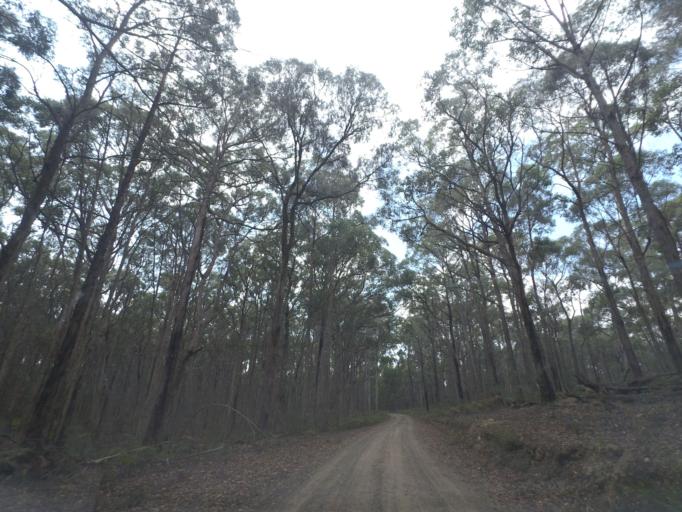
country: AU
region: Victoria
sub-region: Moorabool
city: Bacchus Marsh
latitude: -37.4546
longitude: 144.3559
